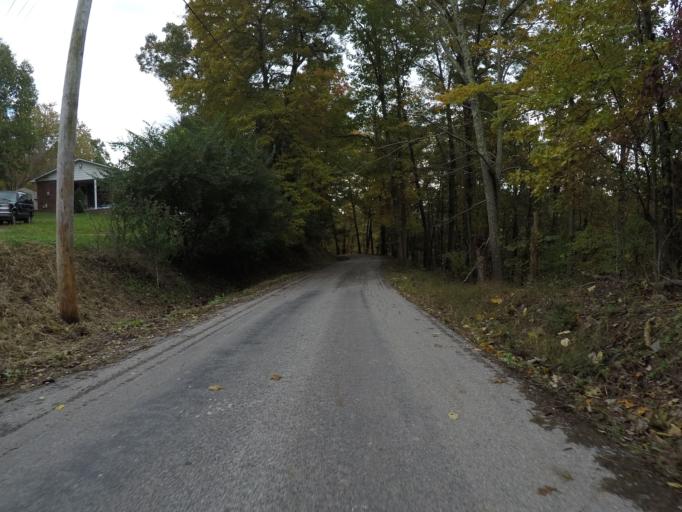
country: US
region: West Virginia
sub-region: Wayne County
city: Lavalette
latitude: 38.3613
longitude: -82.4224
